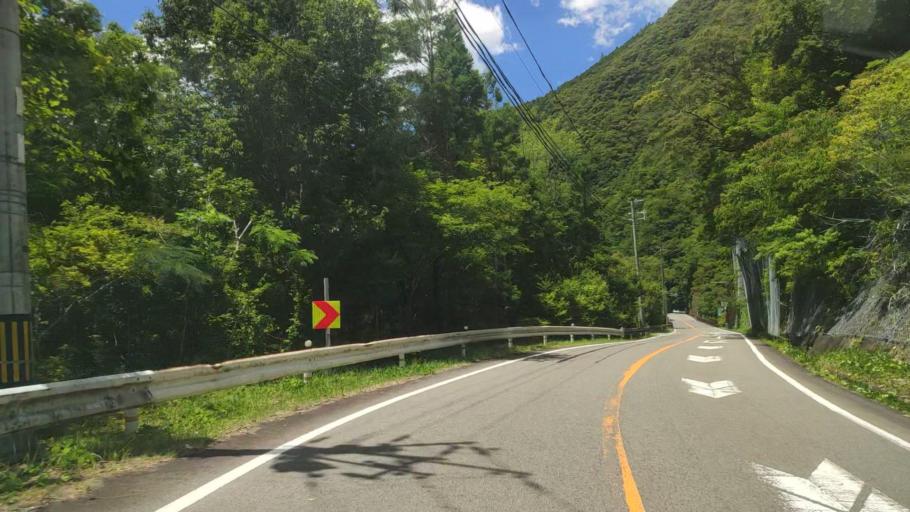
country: JP
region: Mie
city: Owase
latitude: 33.9978
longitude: 136.0182
